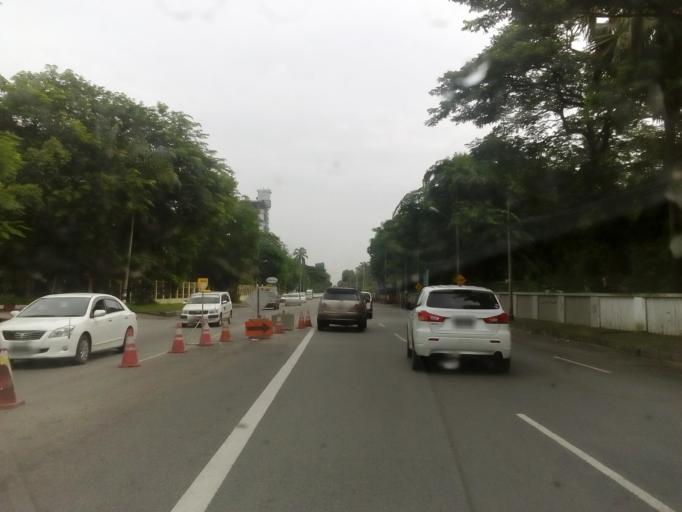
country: MM
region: Yangon
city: Yangon
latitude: 16.8361
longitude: 96.1556
